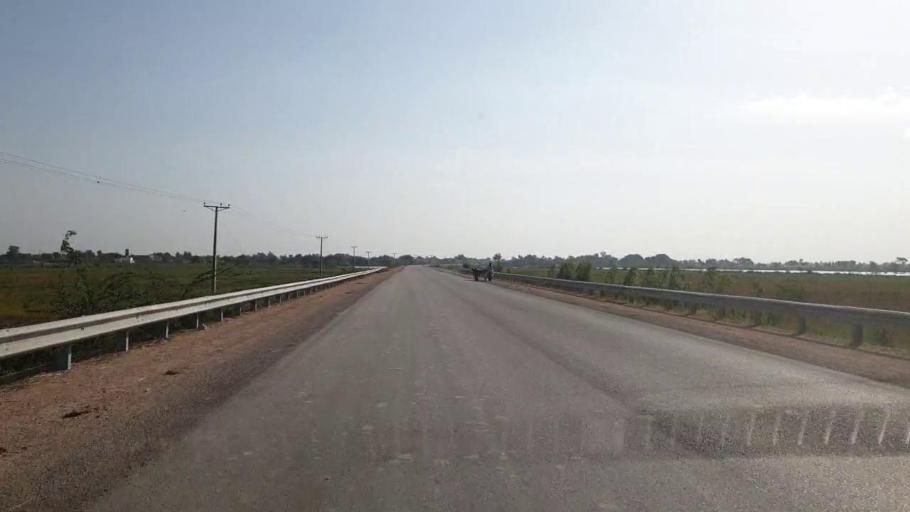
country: PK
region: Sindh
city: Tando Bago
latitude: 24.6567
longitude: 69.0212
